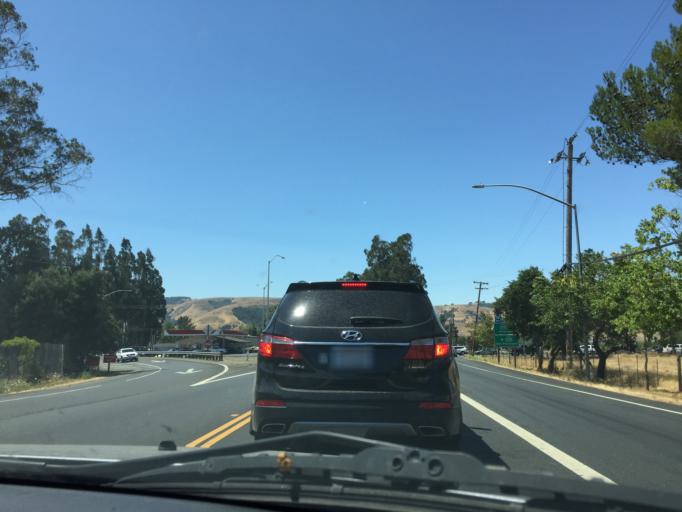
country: US
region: California
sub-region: Sonoma County
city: Temelec
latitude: 38.2366
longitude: -122.4602
